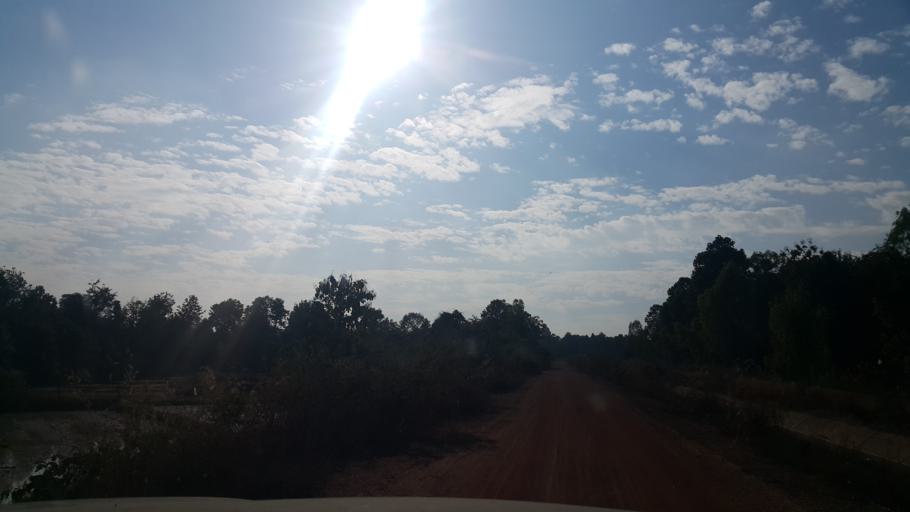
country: TH
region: Lampang
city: Hang Chat
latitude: 18.2614
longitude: 99.3696
